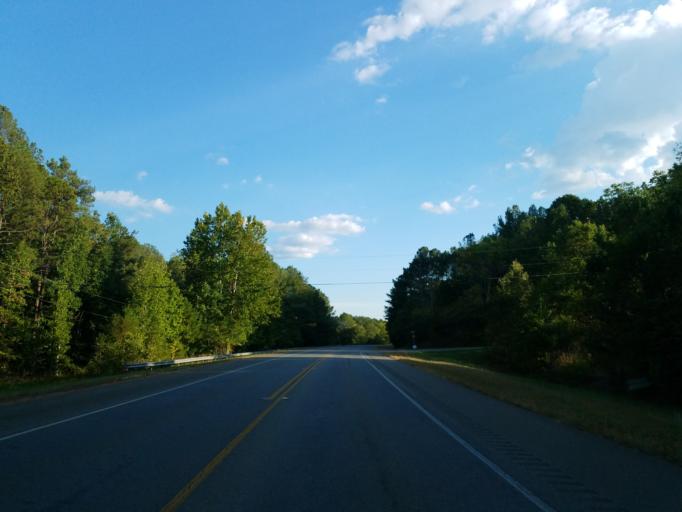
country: US
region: Georgia
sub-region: Murray County
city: Chatsworth
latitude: 34.6419
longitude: -84.7148
